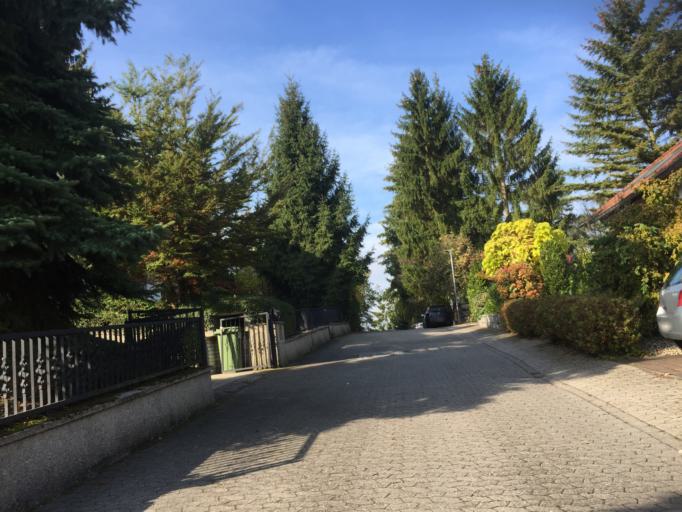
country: DE
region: Hesse
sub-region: Regierungsbezirk Darmstadt
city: Bensheim
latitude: 49.6725
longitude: 8.6453
